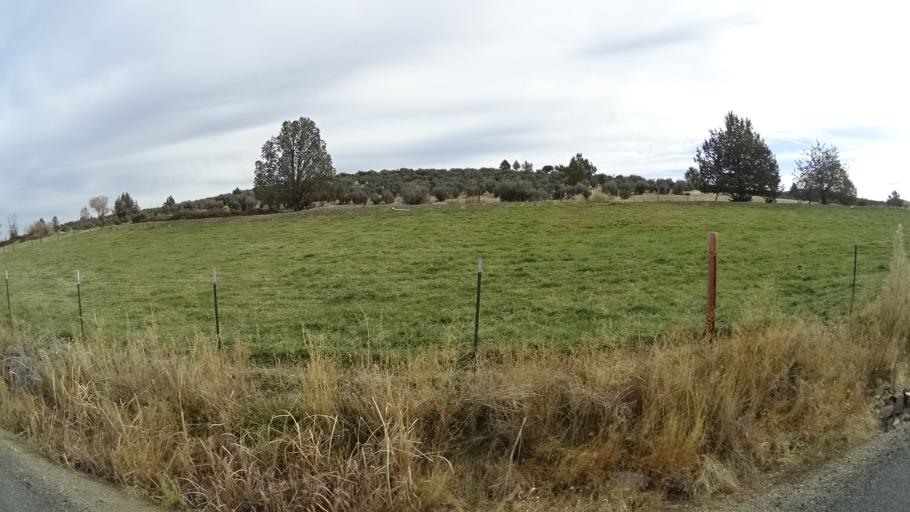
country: US
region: California
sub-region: Siskiyou County
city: Montague
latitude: 41.6957
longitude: -122.5545
